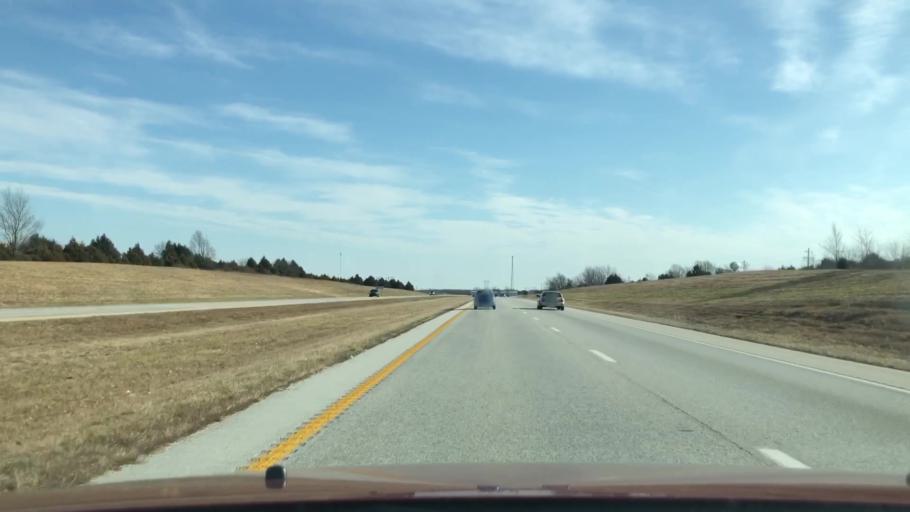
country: US
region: Missouri
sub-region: Webster County
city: Seymour
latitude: 37.1563
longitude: -92.7703
